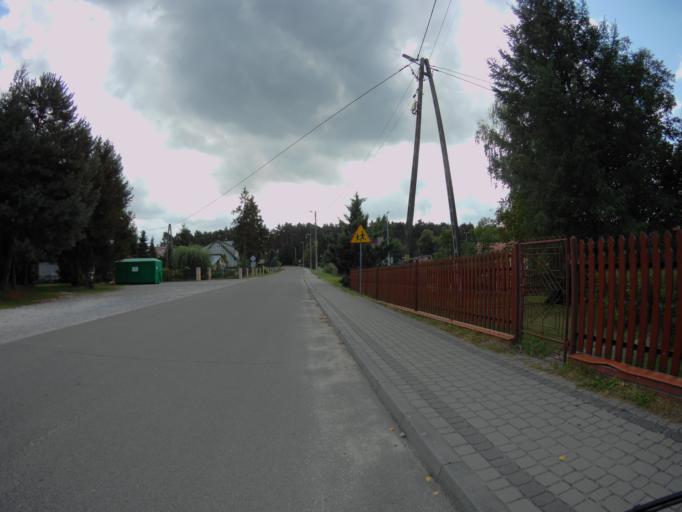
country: PL
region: Subcarpathian Voivodeship
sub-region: Powiat lezajski
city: Brzoza Krolewska
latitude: 50.2446
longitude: 22.3217
